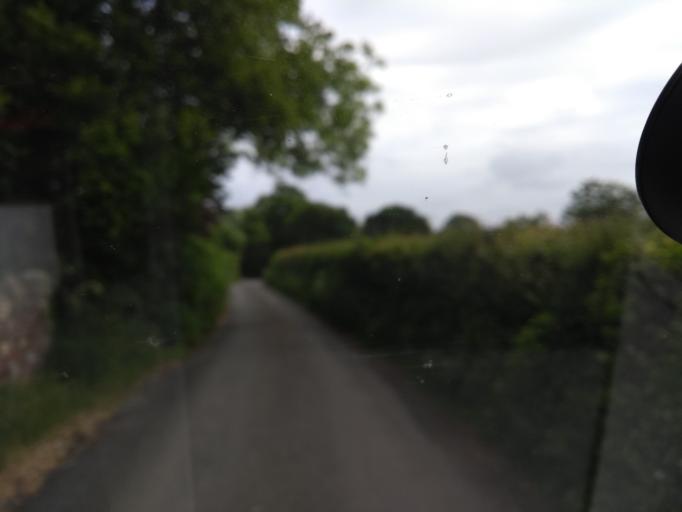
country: GB
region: England
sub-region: Somerset
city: Bishops Lydeard
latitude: 51.1748
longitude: -3.2043
